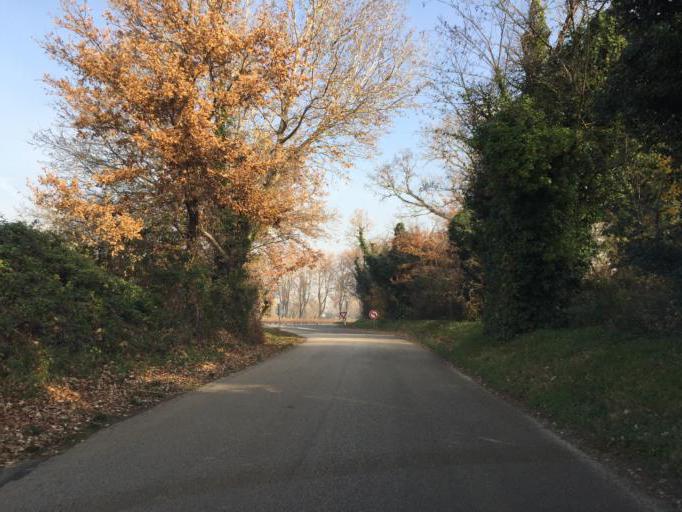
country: FR
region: Provence-Alpes-Cote d'Azur
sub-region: Departement du Vaucluse
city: Jonquieres
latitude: 44.1037
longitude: 4.9141
